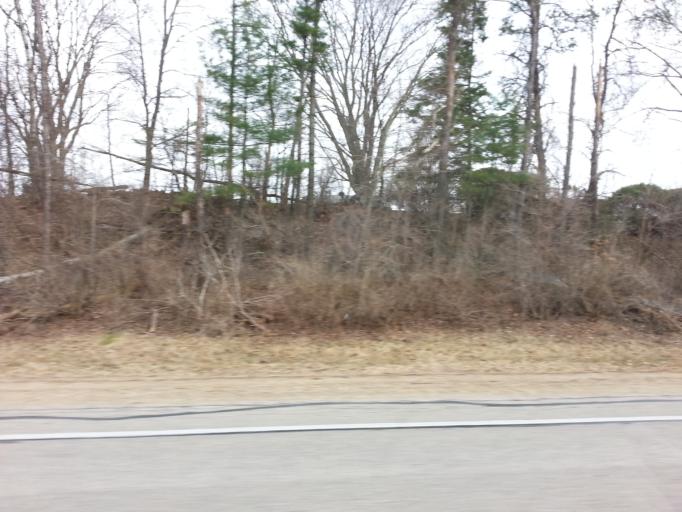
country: US
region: Wisconsin
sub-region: Pierce County
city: Ellsworth
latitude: 44.8290
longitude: -92.4097
